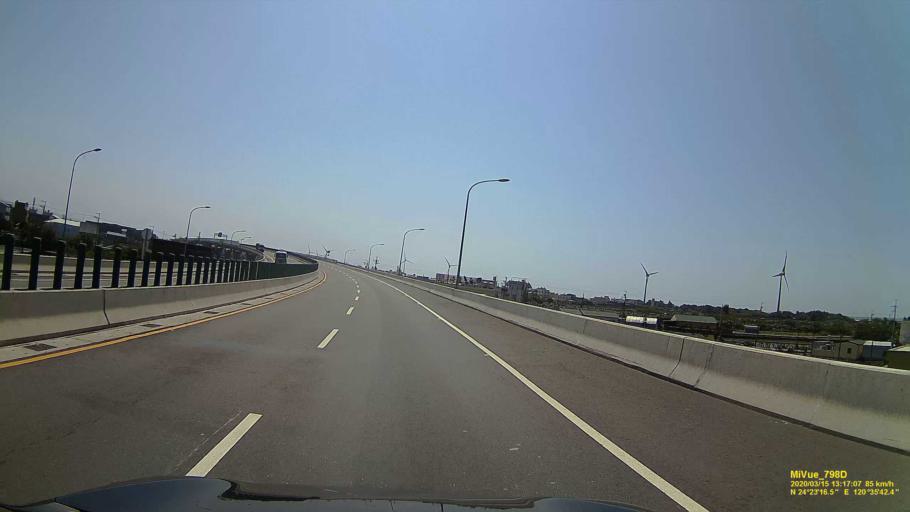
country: TW
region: Taiwan
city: Fengyuan
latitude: 24.3881
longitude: 120.5949
